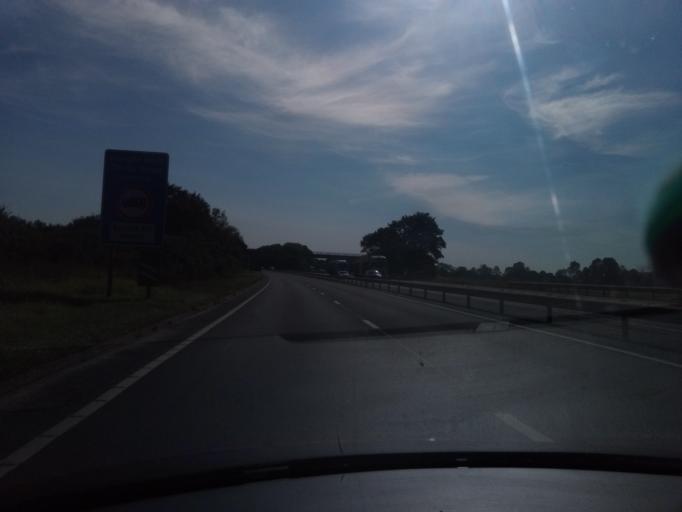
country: GB
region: England
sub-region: North Yorkshire
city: Thirsk
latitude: 54.2423
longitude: -1.3325
